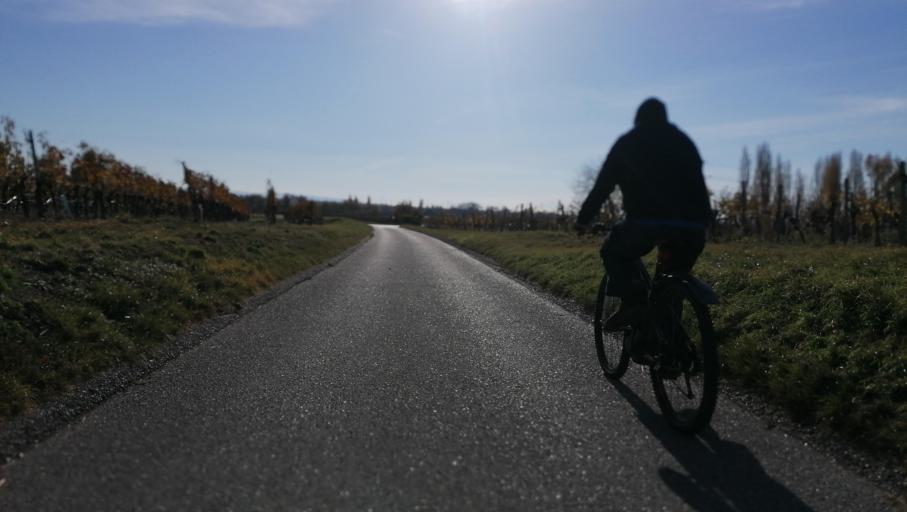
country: AT
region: Lower Austria
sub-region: Politischer Bezirk Modling
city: Gumpoldskirchen
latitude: 48.0358
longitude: 16.2798
